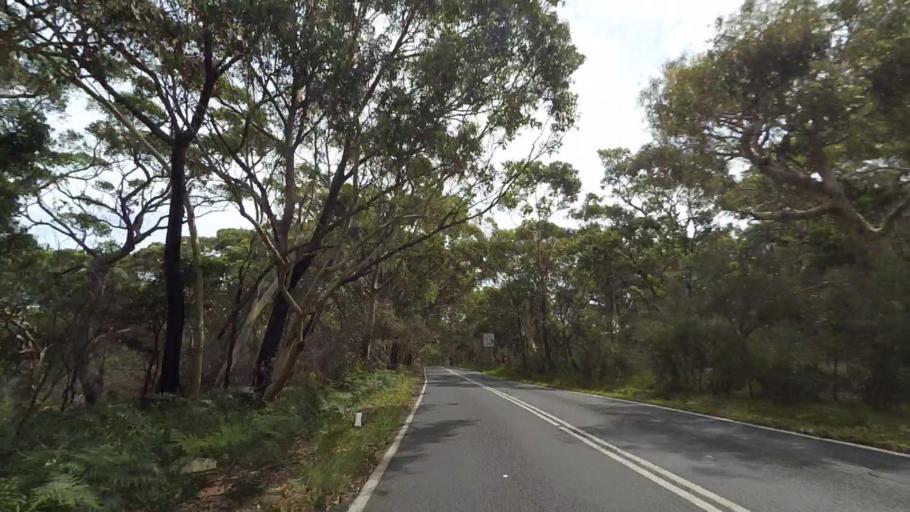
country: AU
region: New South Wales
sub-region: Sutherland Shire
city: Bundeena
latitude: -34.0861
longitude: 151.1417
